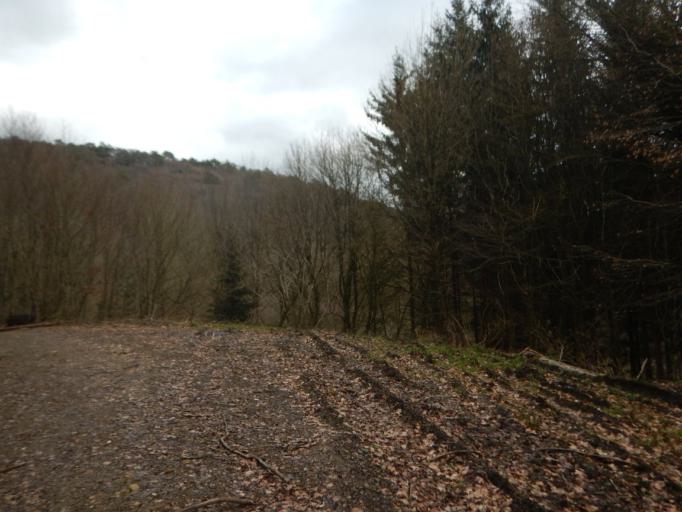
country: LU
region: Luxembourg
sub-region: Canton de Mersch
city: Tuntange
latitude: 49.7169
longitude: 6.0609
